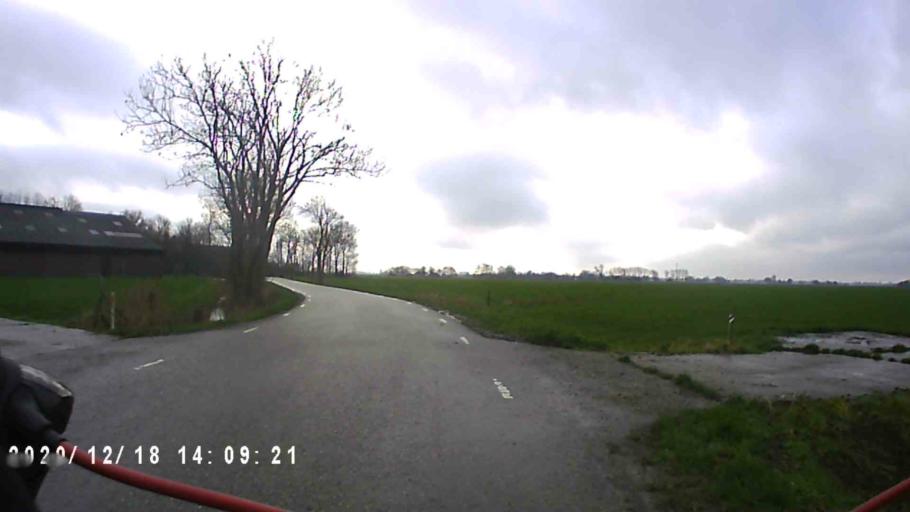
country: NL
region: Groningen
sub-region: Gemeente Bedum
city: Bedum
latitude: 53.2796
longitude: 6.6582
